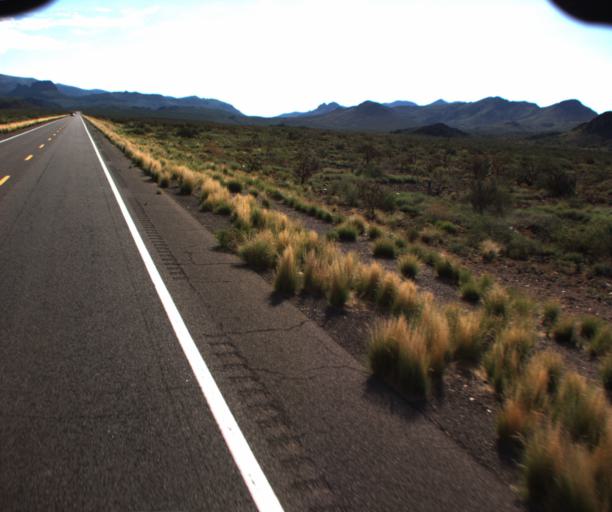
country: US
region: Arizona
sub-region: Greenlee County
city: Morenci
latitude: 32.8367
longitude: -109.4351
